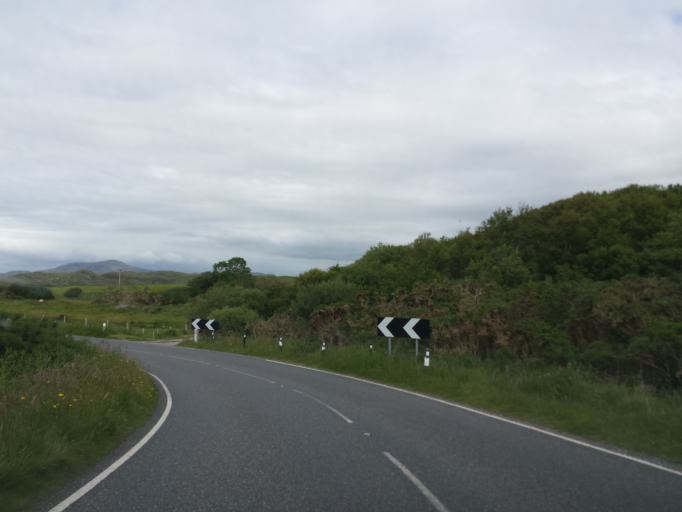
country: GB
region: Scotland
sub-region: Argyll and Bute
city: Isle Of Mull
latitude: 56.9360
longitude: -5.8596
